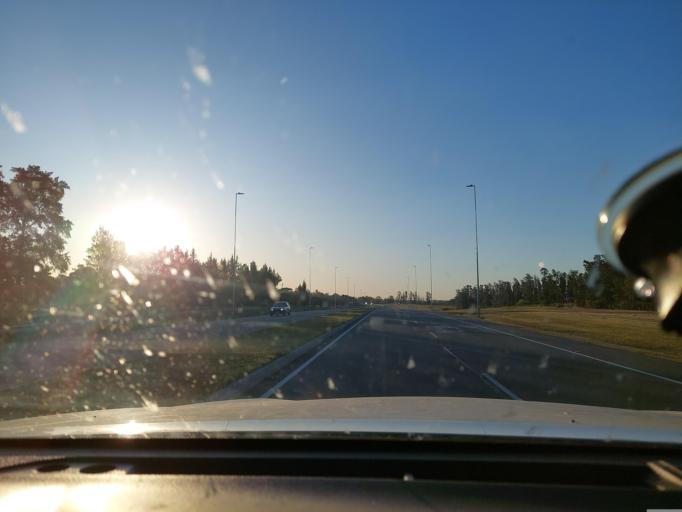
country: UY
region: Canelones
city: Empalme Olmos
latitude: -34.7009
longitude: -55.9076
